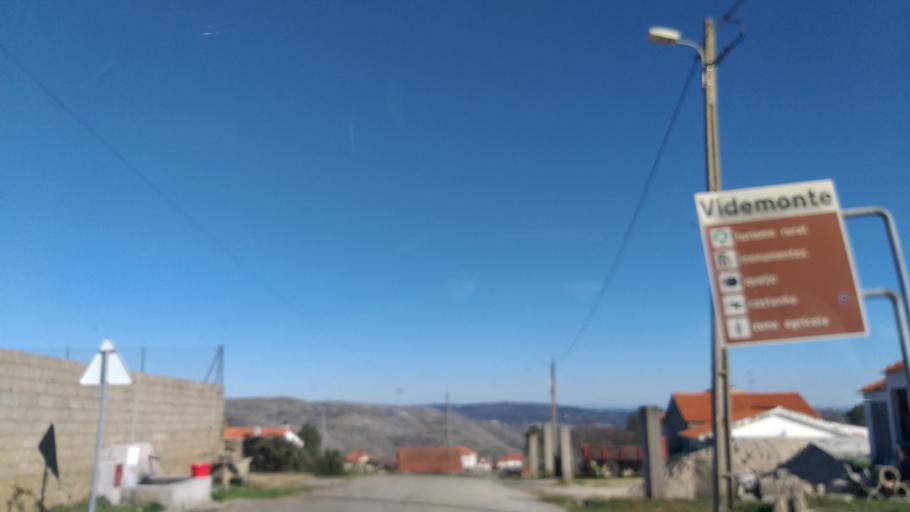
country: PT
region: Guarda
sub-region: Celorico da Beira
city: Celorico da Beira
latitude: 40.5169
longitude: -7.4019
